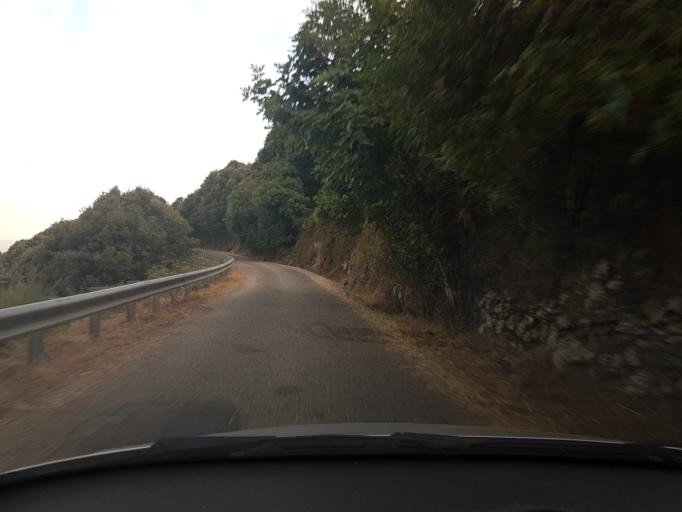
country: IT
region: Sardinia
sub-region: Provincia di Oristano
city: Seneghe
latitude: 40.1105
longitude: 8.6061
